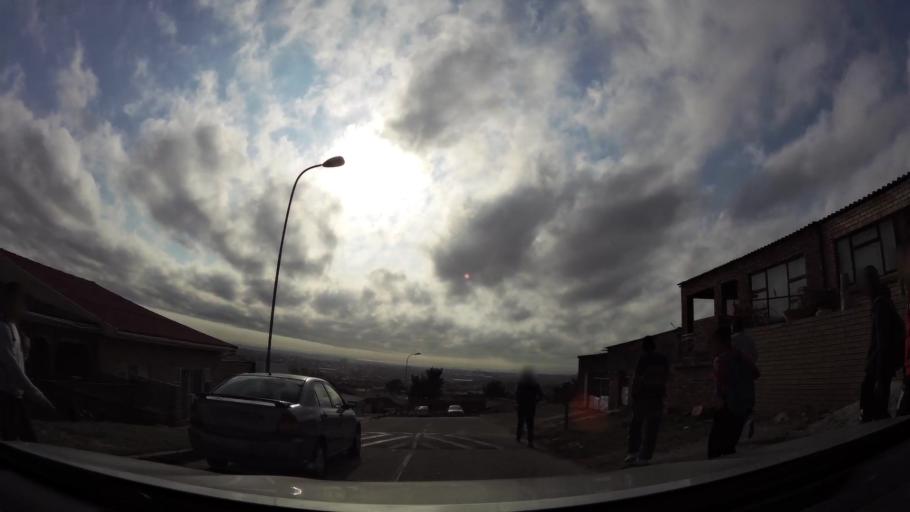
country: ZA
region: Eastern Cape
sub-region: Nelson Mandela Bay Metropolitan Municipality
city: Port Elizabeth
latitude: -33.9202
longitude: 25.5484
